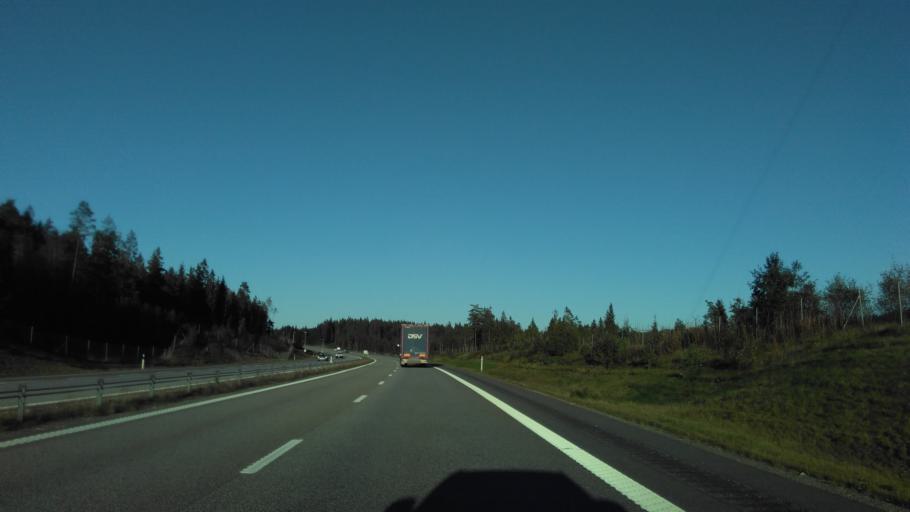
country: SE
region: Vaestra Goetaland
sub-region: Boras Kommun
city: Dalsjofors
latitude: 57.7413
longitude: 13.0567
